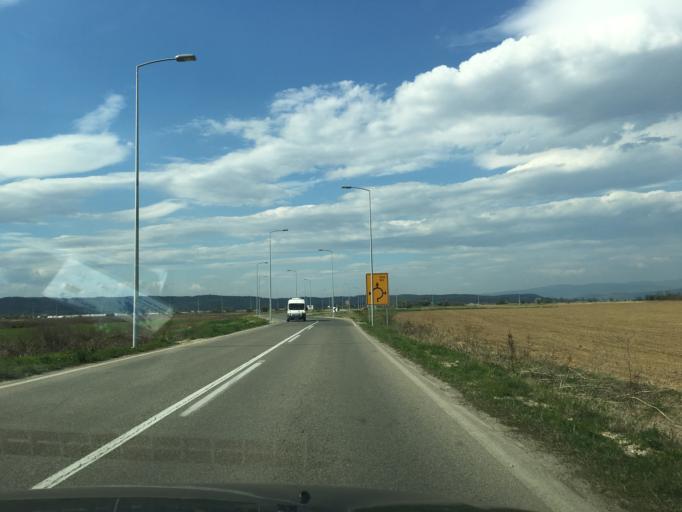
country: RS
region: Central Serbia
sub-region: Jablanicki Okrug
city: Leskovac
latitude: 43.0256
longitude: 21.9460
